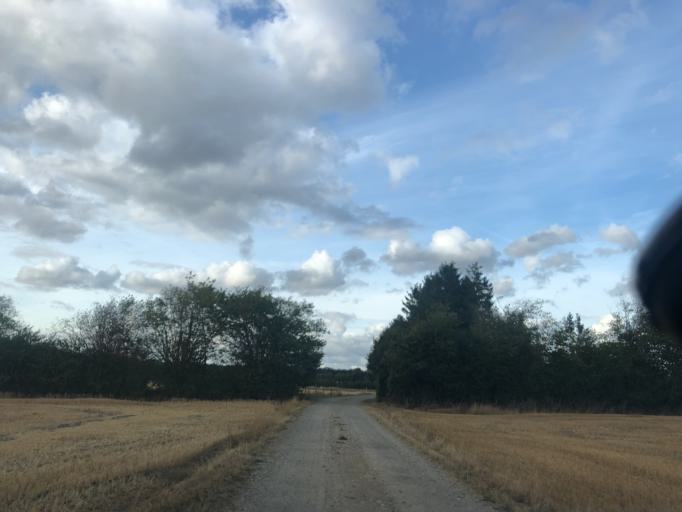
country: DK
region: Zealand
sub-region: Koge Kommune
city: Bjaeverskov
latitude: 55.4029
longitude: 12.0741
